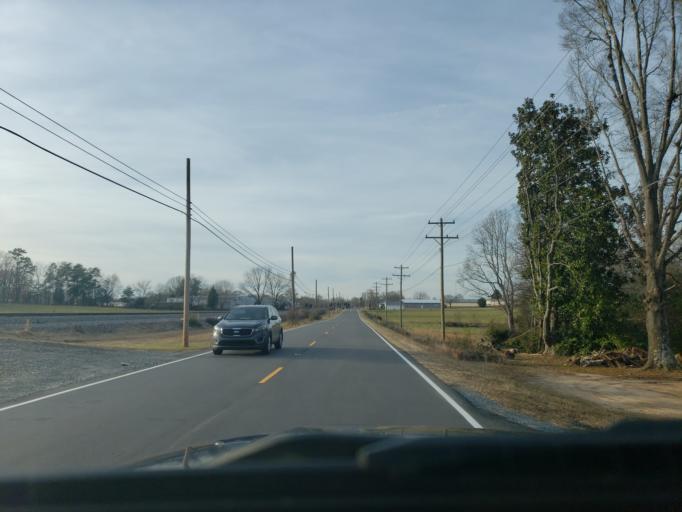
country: US
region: North Carolina
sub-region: Cleveland County
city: Boiling Springs
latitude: 35.3203
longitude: -81.7498
